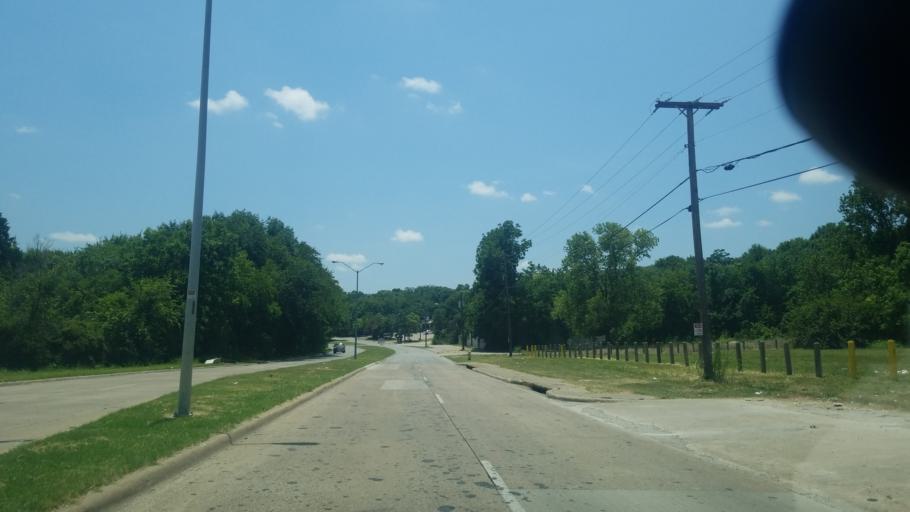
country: US
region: Texas
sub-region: Dallas County
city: Dallas
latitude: 32.7288
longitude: -96.7855
